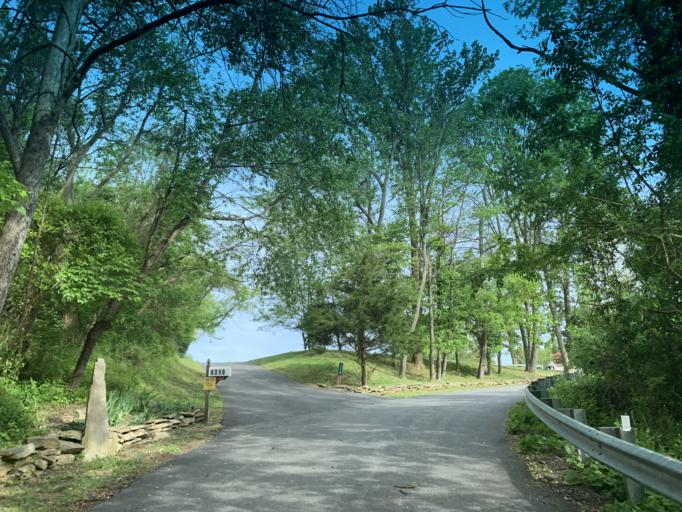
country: US
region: Maryland
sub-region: Baltimore County
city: Perry Hall
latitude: 39.4494
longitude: -76.4611
